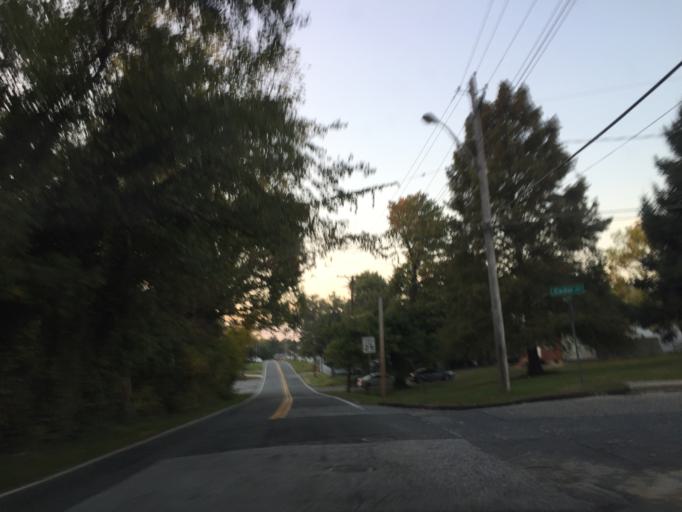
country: US
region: Maryland
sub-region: Baltimore County
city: Essex
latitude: 39.3022
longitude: -76.4753
